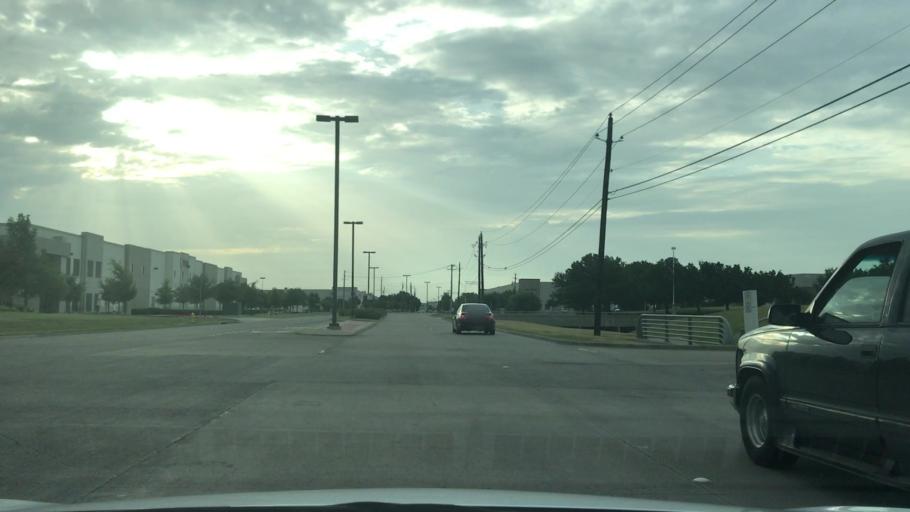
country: US
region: Texas
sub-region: Dallas County
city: Coppell
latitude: 32.9550
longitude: -97.0193
